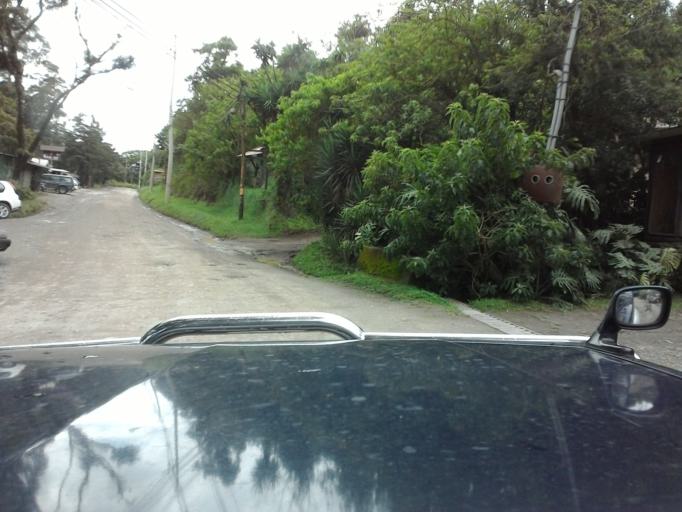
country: CR
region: Guanacaste
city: Juntas
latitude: 10.3070
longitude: -84.8117
